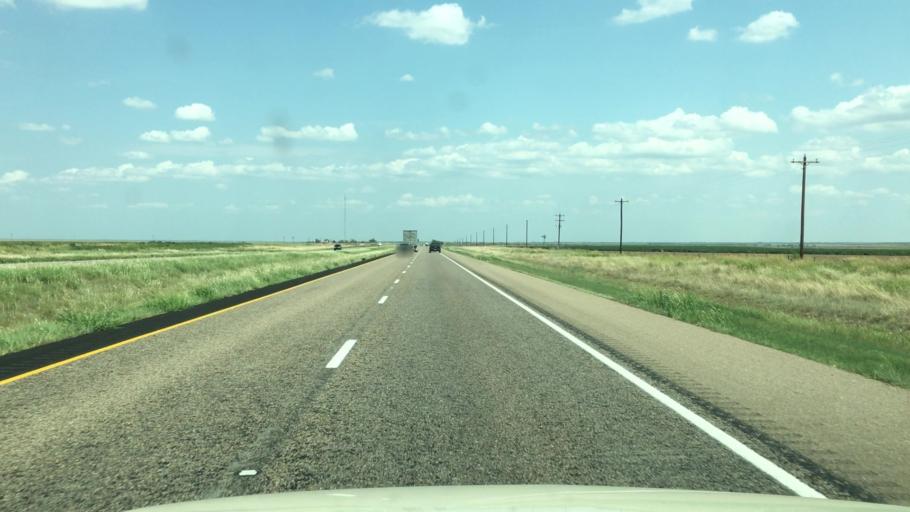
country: US
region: Texas
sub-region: Armstrong County
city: Claude
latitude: 35.0334
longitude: -101.1684
